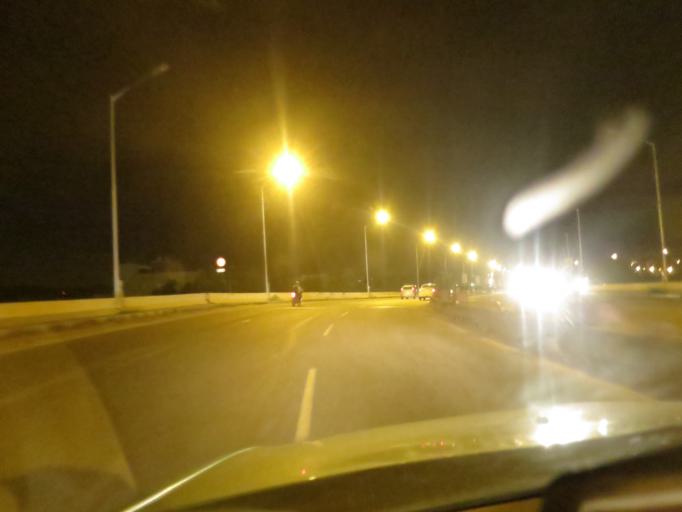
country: IN
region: Karnataka
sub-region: Bangalore Urban
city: Bangalore
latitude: 12.9981
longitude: 77.6636
